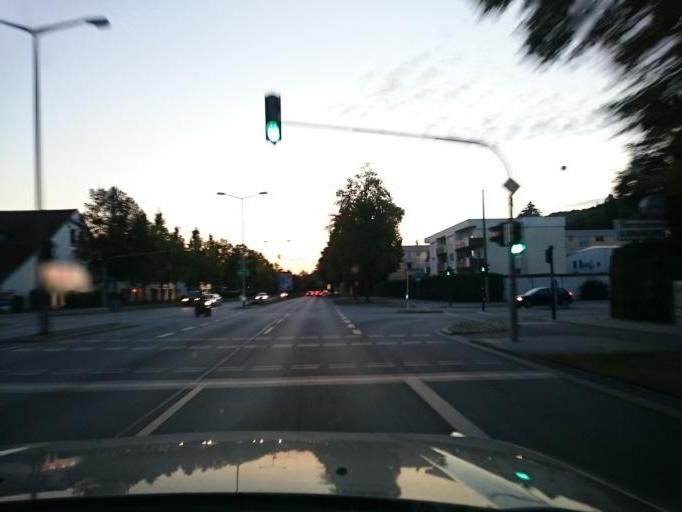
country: DE
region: Bavaria
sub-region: Upper Palatinate
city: Lappersdorf
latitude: 49.0285
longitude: 12.0895
